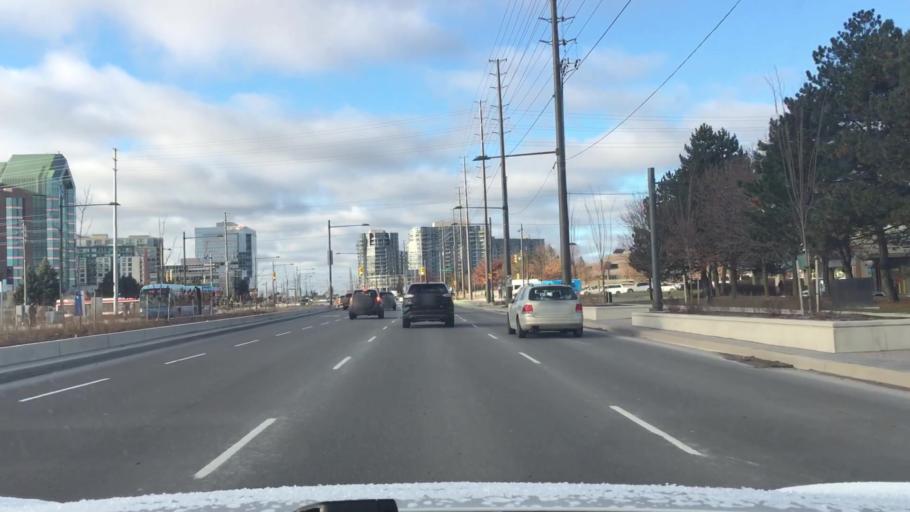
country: CA
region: Ontario
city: Markham
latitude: 43.8562
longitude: -79.3324
